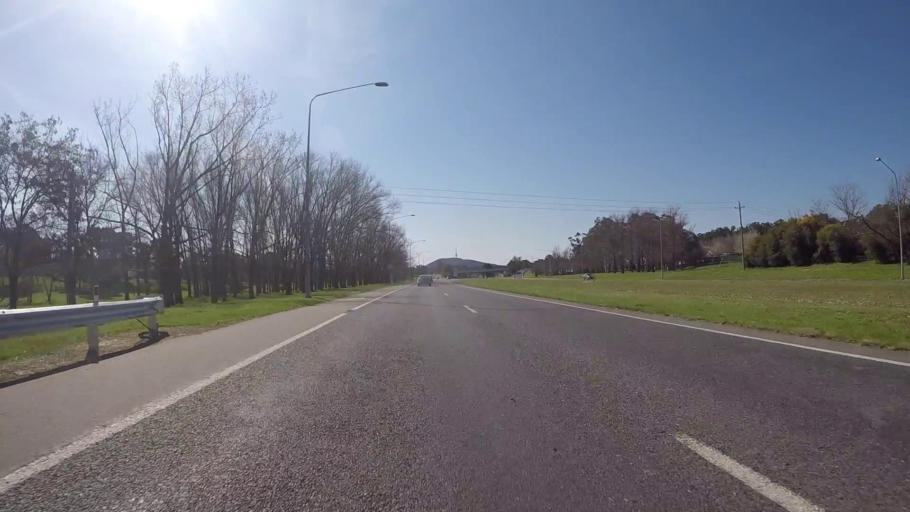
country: AU
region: Australian Capital Territory
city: Forrest
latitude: -35.3305
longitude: 149.0860
